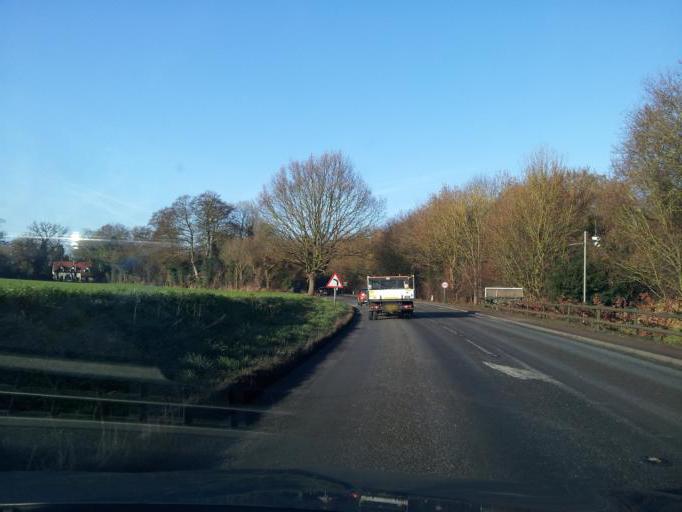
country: GB
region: England
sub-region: Suffolk
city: Bury St Edmunds
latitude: 52.2058
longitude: 0.7558
